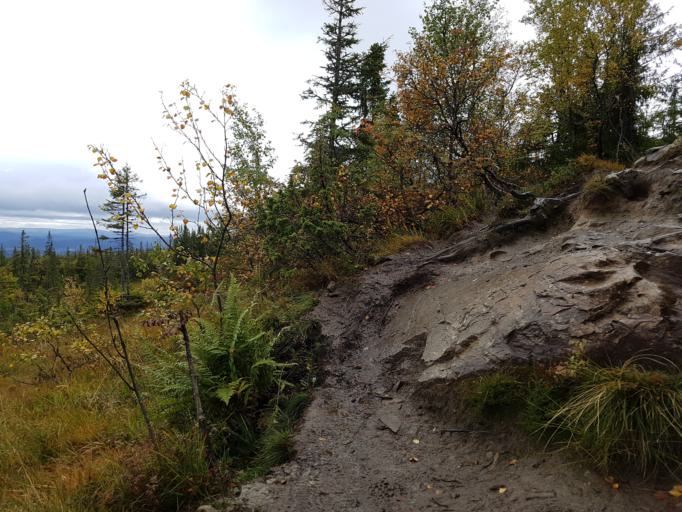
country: NO
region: Sor-Trondelag
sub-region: Melhus
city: Melhus
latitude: 63.4082
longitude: 10.2059
